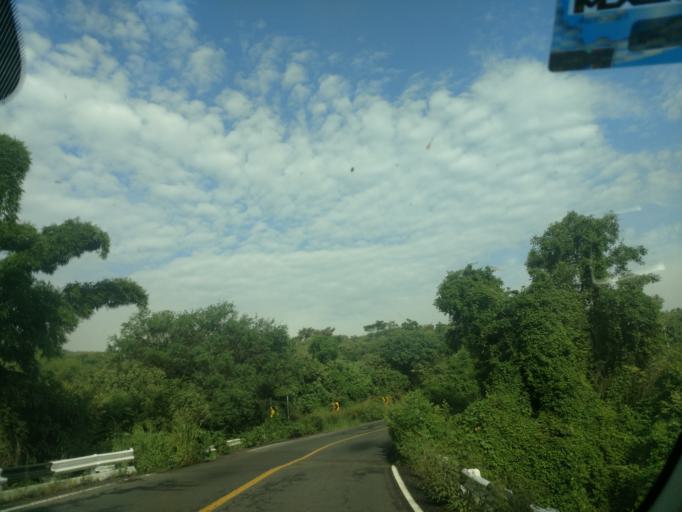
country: MX
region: Jalisco
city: Ameca
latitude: 20.5288
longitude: -104.1309
